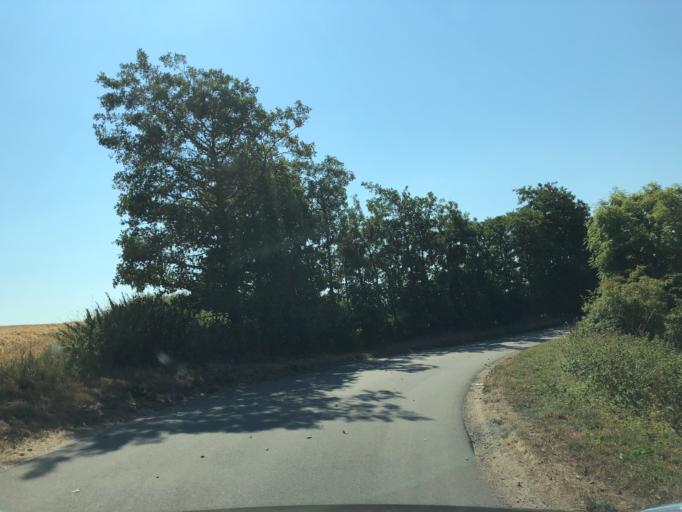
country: DK
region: Zealand
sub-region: Odsherred Kommune
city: Hojby
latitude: 55.9550
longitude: 11.4885
